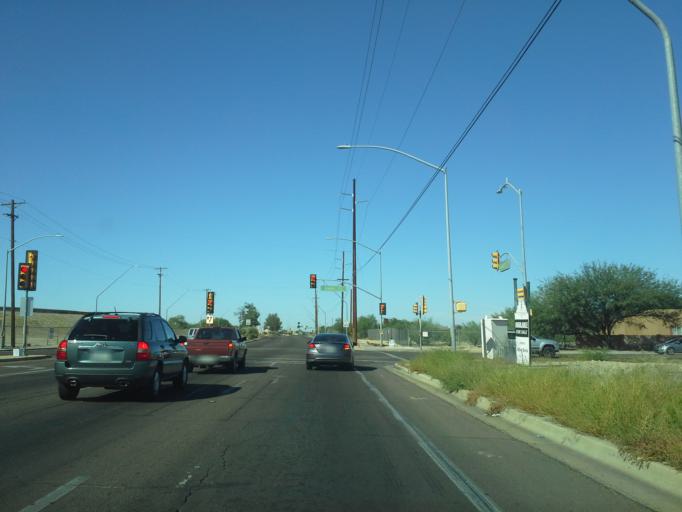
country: US
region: Arizona
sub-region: Pima County
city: South Tucson
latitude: 32.1342
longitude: -110.9557
